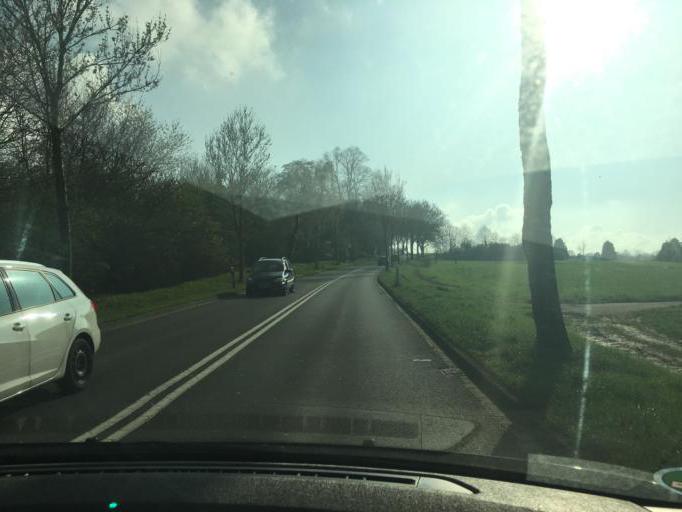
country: DE
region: North Rhine-Westphalia
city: Bornheim
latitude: 50.7596
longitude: 6.9701
